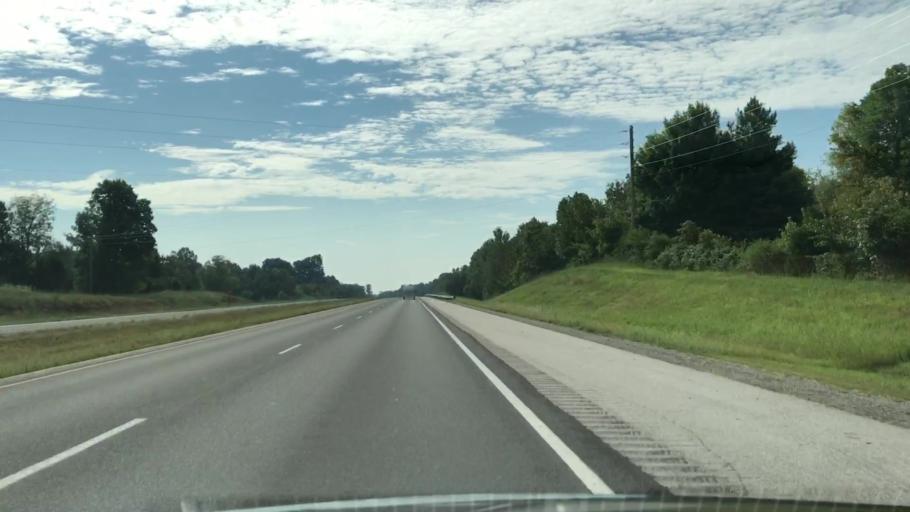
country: US
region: Kentucky
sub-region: Warren County
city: Plano
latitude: 36.8538
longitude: -86.3376
